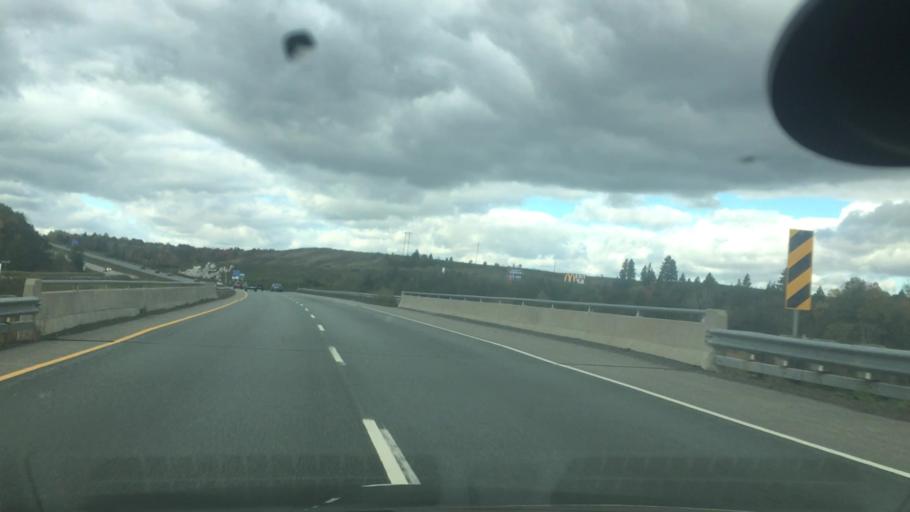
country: CA
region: Nova Scotia
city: Windsor
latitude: 44.9676
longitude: -64.0299
